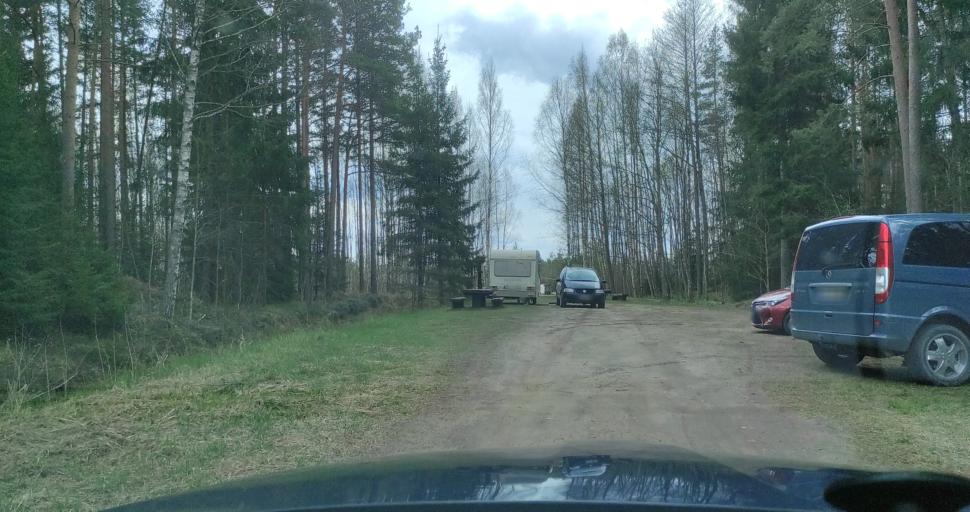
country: LV
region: Dundaga
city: Dundaga
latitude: 57.3572
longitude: 22.1534
